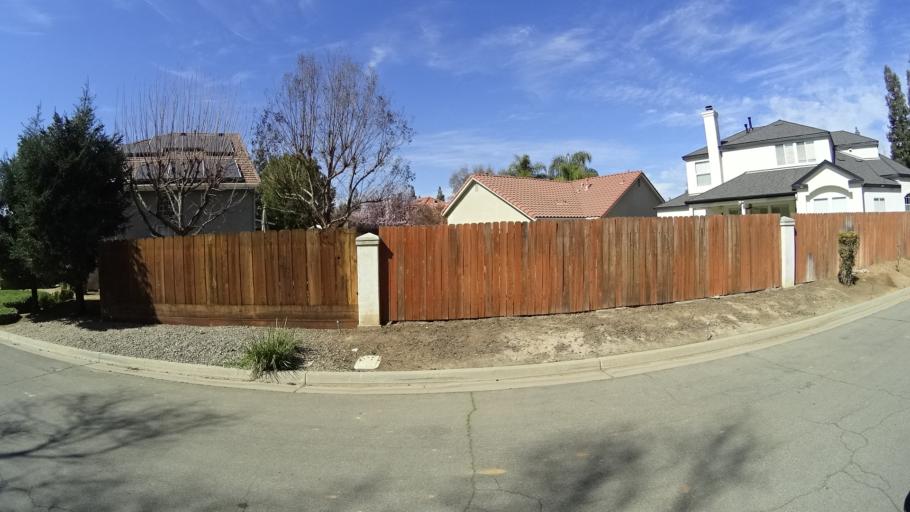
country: US
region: California
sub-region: Fresno County
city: Clovis
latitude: 36.8547
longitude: -119.7640
